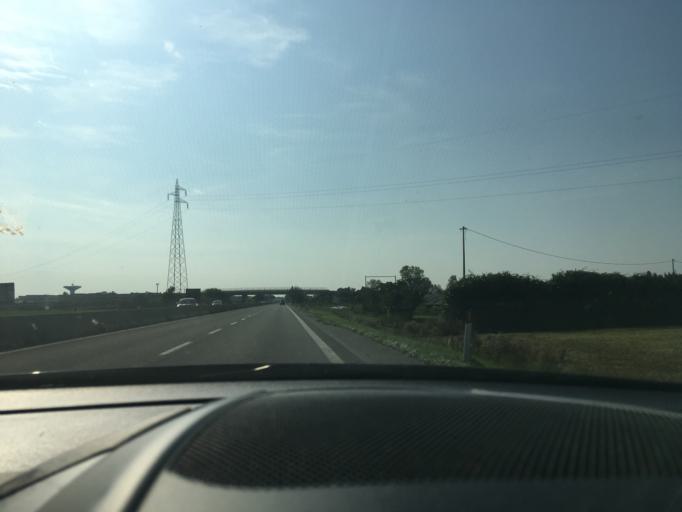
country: IT
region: Emilia-Romagna
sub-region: Provincia di Rimini
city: Bellaria-Igea Marina
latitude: 44.1355
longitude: 12.4627
